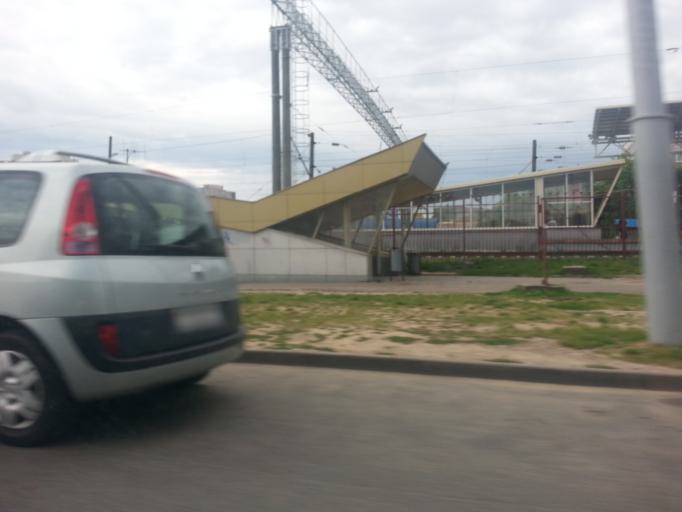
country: BY
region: Minsk
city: Minsk
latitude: 53.8853
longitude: 27.5392
